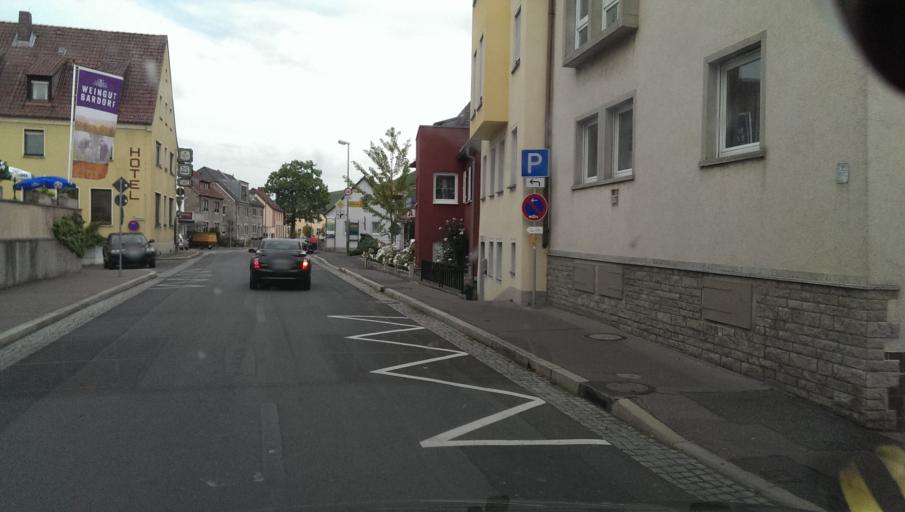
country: DE
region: Bavaria
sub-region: Regierungsbezirk Unterfranken
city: Randersacker
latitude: 49.7577
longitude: 9.9817
